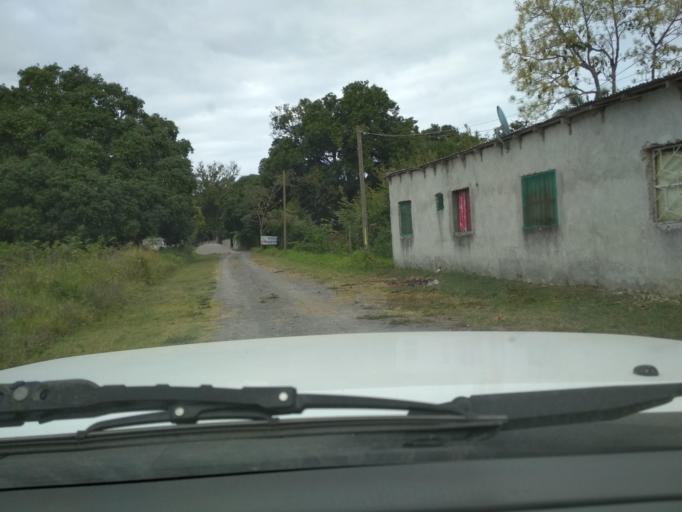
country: MX
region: Veracruz
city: El Tejar
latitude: 19.0738
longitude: -96.1443
